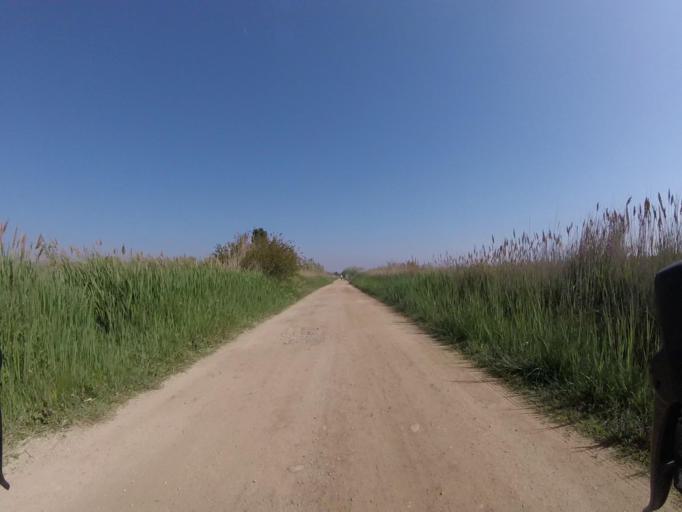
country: ES
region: Valencia
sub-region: Provincia de Castello
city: Orpesa/Oropesa del Mar
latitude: 40.1426
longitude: 0.1639
